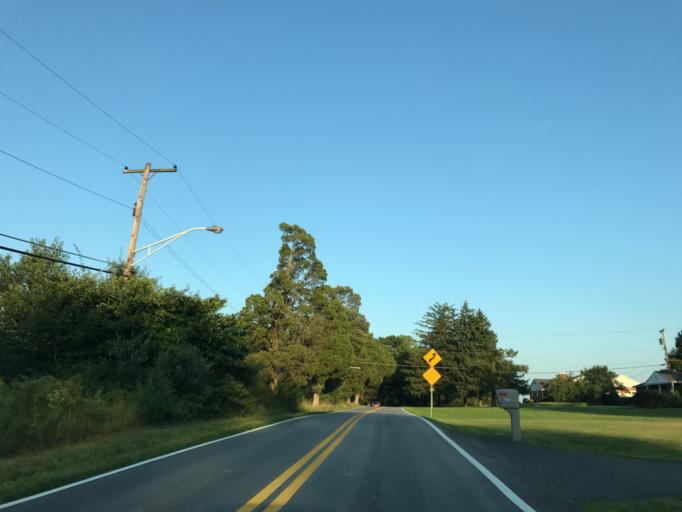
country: US
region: Maryland
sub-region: Baltimore County
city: Kingsville
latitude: 39.4316
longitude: -76.4217
